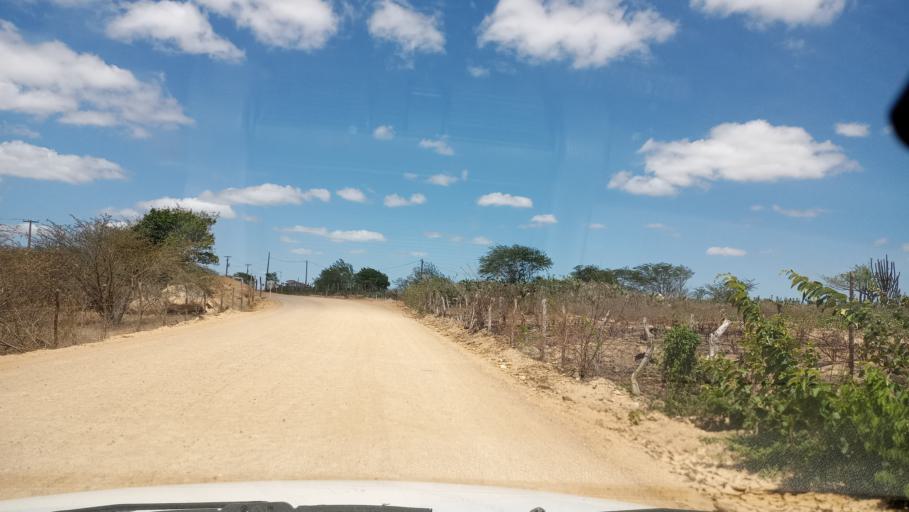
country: BR
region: Rio Grande do Norte
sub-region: Sao Paulo Do Potengi
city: Sao Paulo do Potengi
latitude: -5.7866
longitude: -35.9156
